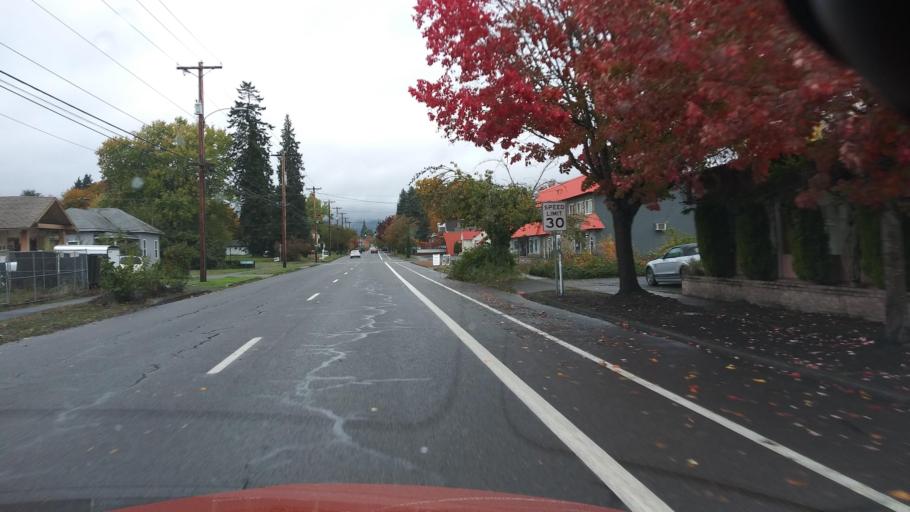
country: US
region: Oregon
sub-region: Washington County
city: Forest Grove
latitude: 45.5196
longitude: -123.0998
